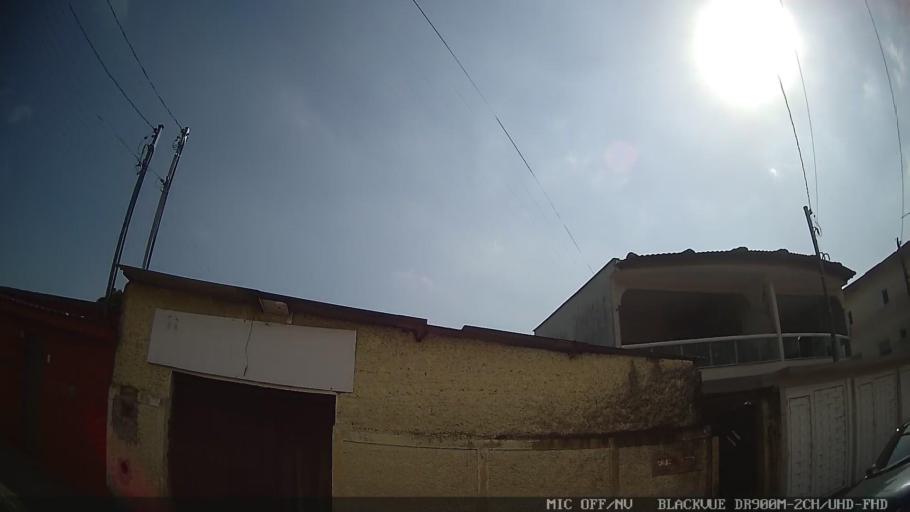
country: BR
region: Sao Paulo
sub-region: Santos
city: Santos
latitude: -23.9402
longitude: -46.3022
